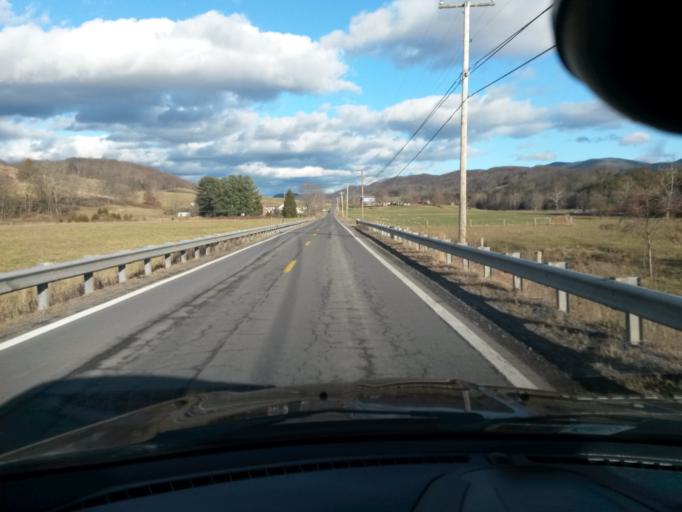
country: US
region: Virginia
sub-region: Giles County
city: Pearisburg
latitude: 37.4299
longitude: -80.7159
